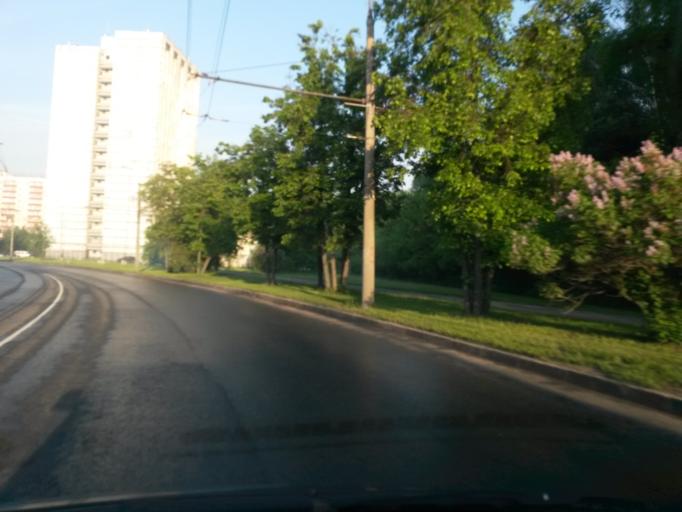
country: RU
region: Moscow
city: Gol'yanovo
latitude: 55.8229
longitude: 37.8011
